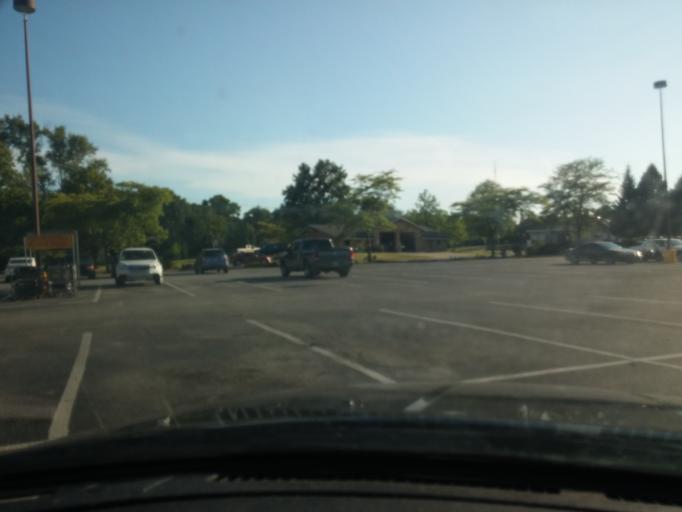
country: US
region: Indiana
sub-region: Tippecanoe County
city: West Lafayette
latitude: 40.4523
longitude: -86.9145
